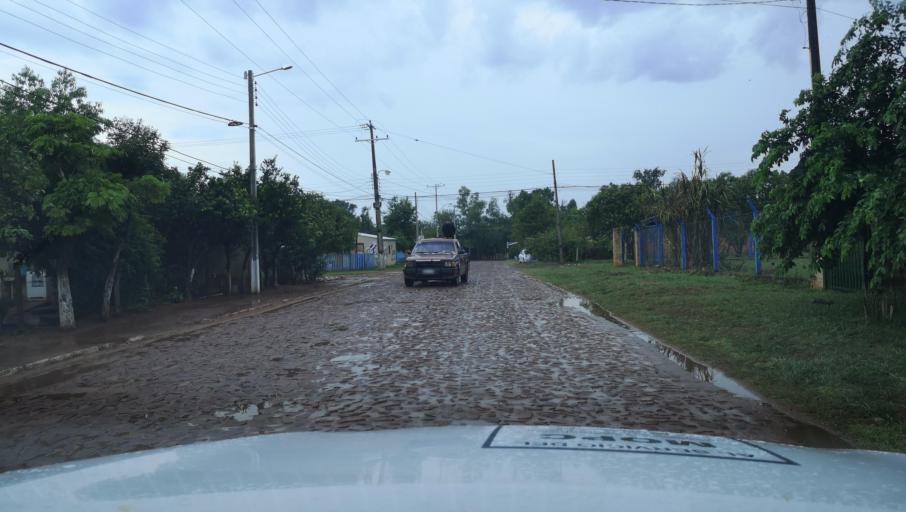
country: PY
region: Misiones
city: Santa Maria
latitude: -26.8959
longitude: -57.0325
